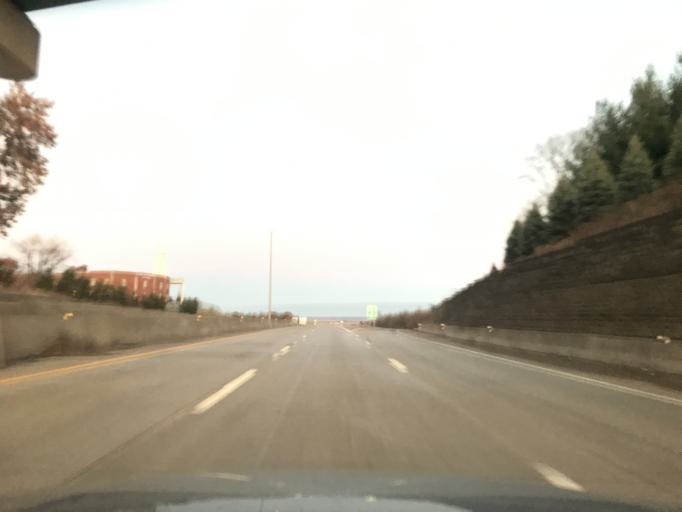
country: US
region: Missouri
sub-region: Marion County
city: Hannibal
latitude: 39.7161
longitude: -91.3781
